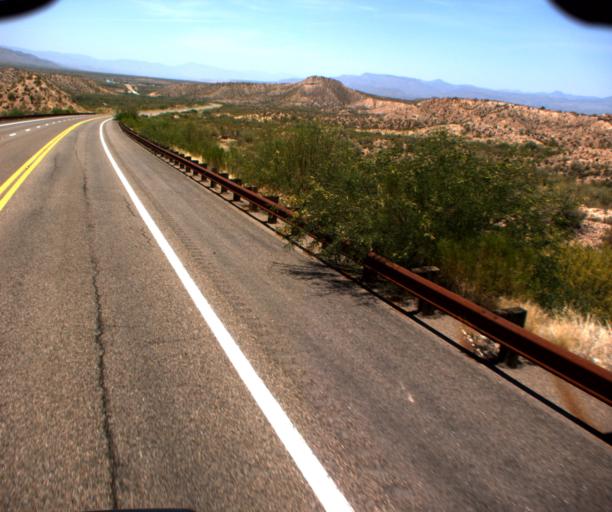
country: US
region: Arizona
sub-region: Gila County
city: Miami
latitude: 33.5850
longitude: -110.9789
